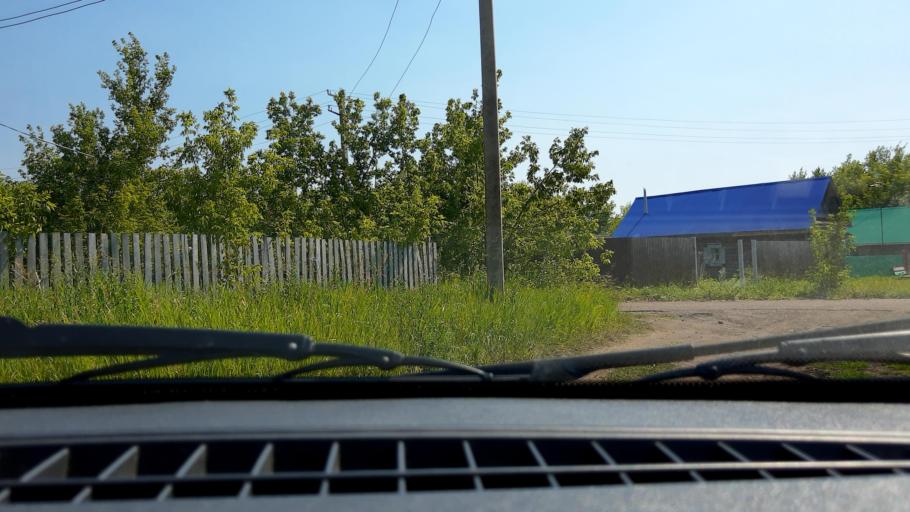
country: RU
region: Bashkortostan
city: Kushnarenkovo
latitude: 55.0756
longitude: 55.1704
